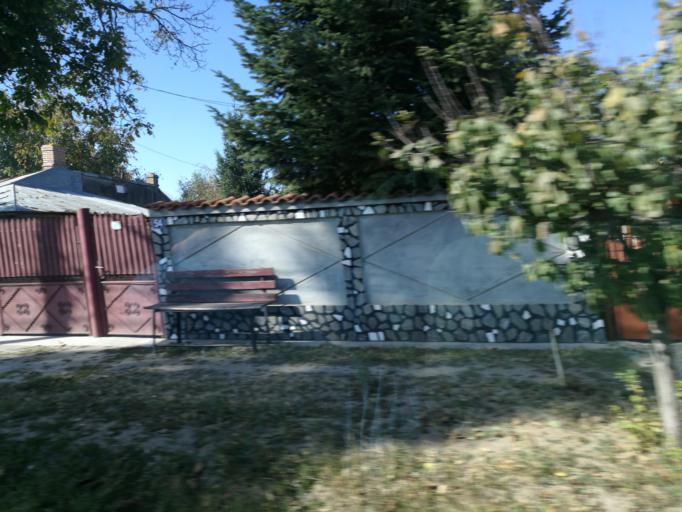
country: RO
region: Giurgiu
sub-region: Comuna Joita
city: Bacu
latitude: 44.4770
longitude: 25.8910
